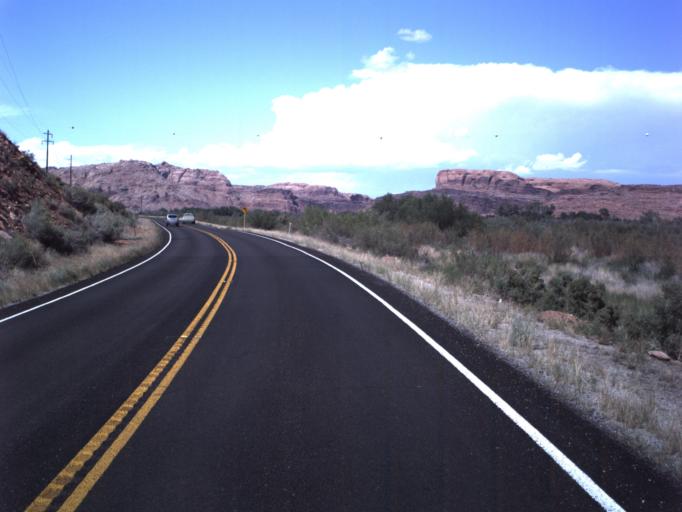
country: US
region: Utah
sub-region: Grand County
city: Moab
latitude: 38.5729
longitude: -109.5802
